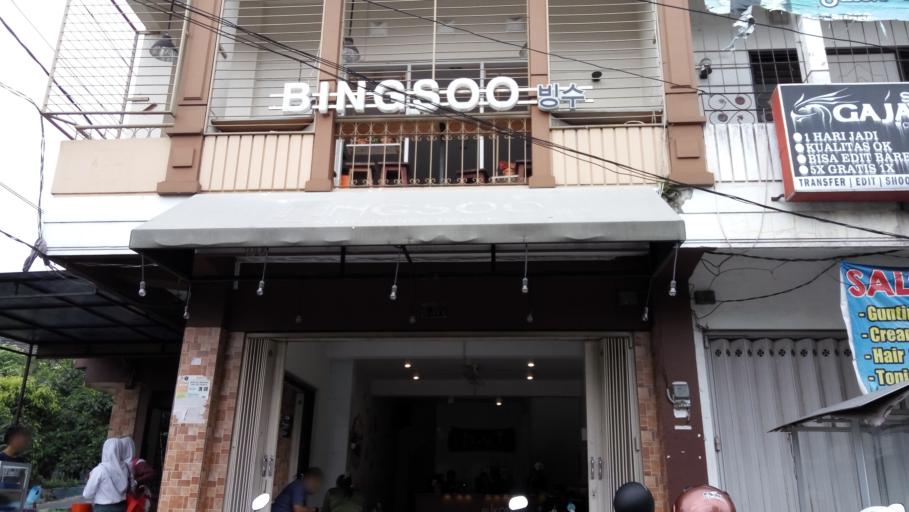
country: ID
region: East Java
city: Malang
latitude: -7.9609
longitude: 112.6136
